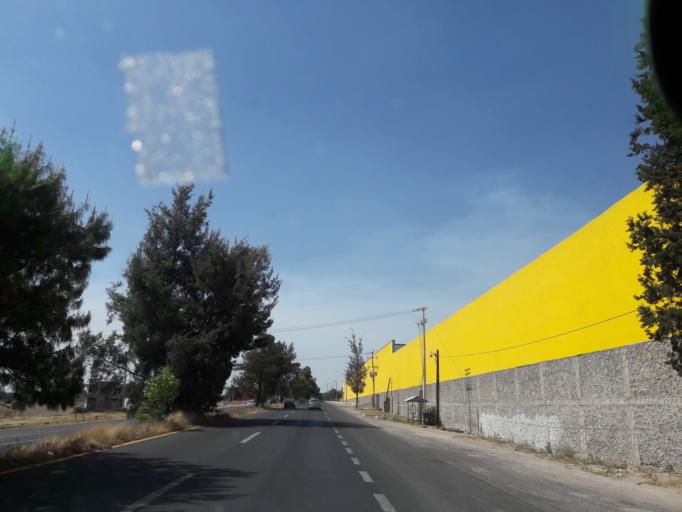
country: MX
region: Tlaxcala
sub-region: Mazatecochco de Jose Maria Morelos
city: Mazatecochco
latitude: 19.1869
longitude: -98.1936
